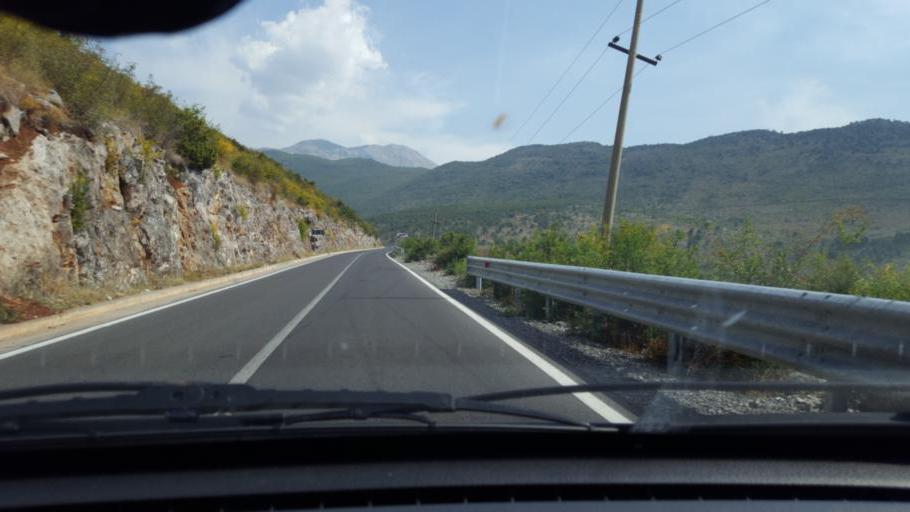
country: AL
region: Shkoder
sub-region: Rrethi i Malesia e Madhe
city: Hot
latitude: 42.3747
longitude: 19.4542
